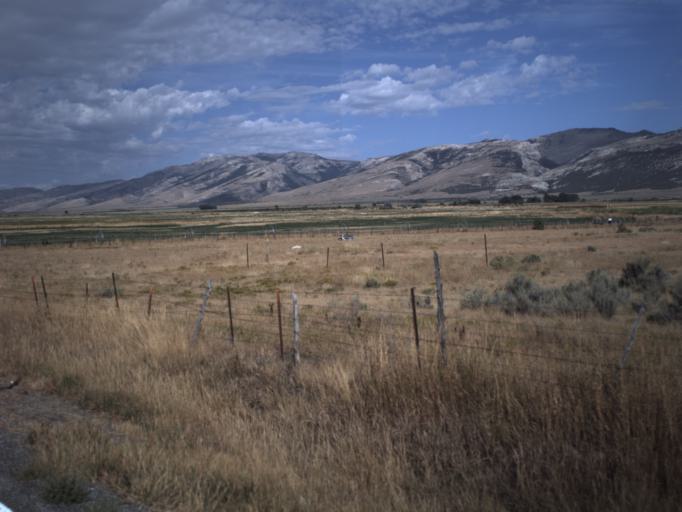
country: US
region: Idaho
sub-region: Cassia County
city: Burley
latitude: 41.8170
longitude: -113.3340
